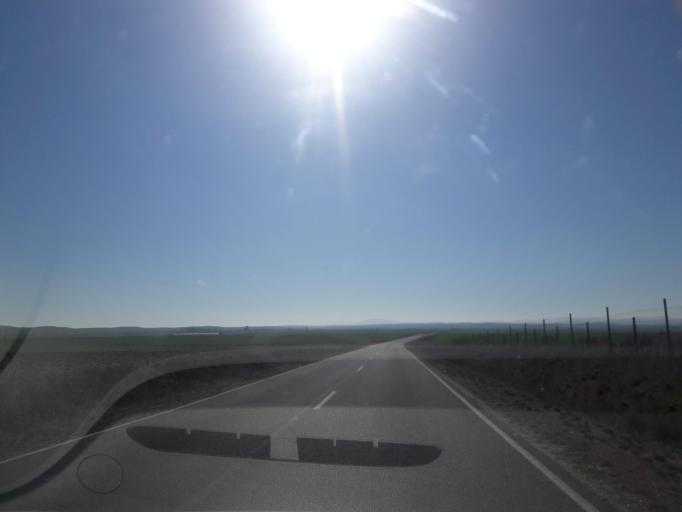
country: ES
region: Castille and Leon
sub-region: Provincia de Salamanca
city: Santiago de la Puebla
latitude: 40.8140
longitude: -5.2569
